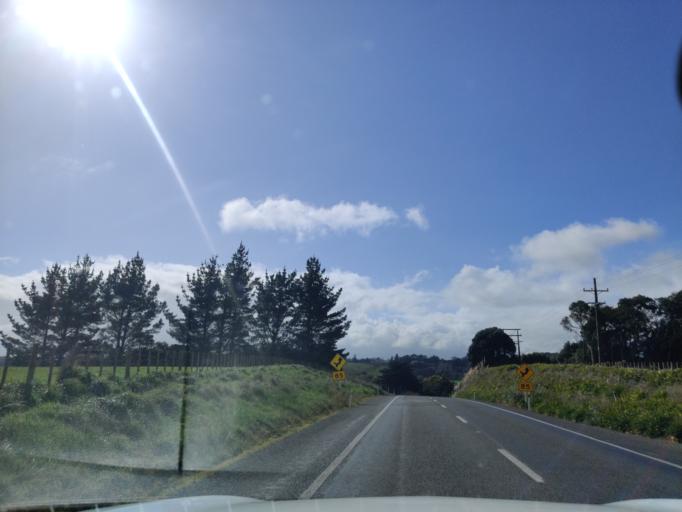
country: NZ
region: Manawatu-Wanganui
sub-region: Palmerston North City
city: Palmerston North
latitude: -40.3962
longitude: 175.6269
